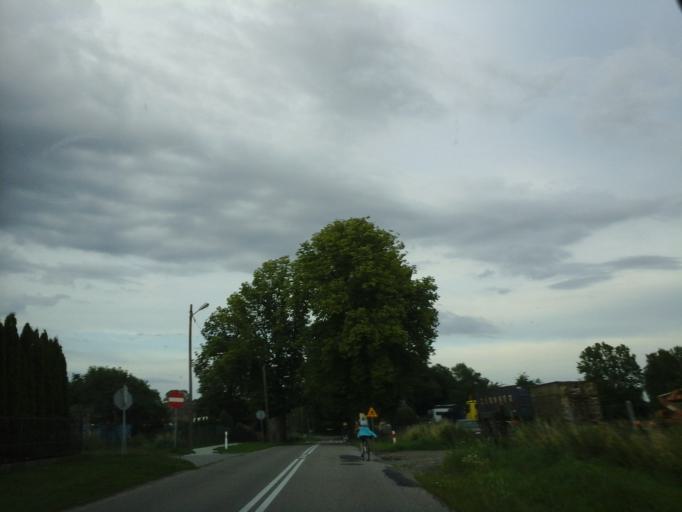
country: PL
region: West Pomeranian Voivodeship
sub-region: Powiat goleniowski
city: Nowogard
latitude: 53.6903
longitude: 15.0750
